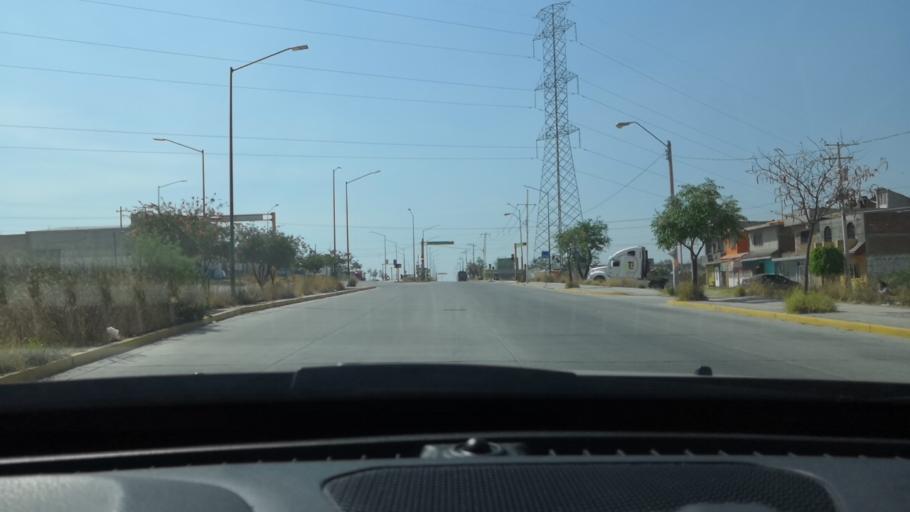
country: MX
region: Guanajuato
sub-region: Leon
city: Ejido la Joya
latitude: 21.1390
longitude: -101.7355
